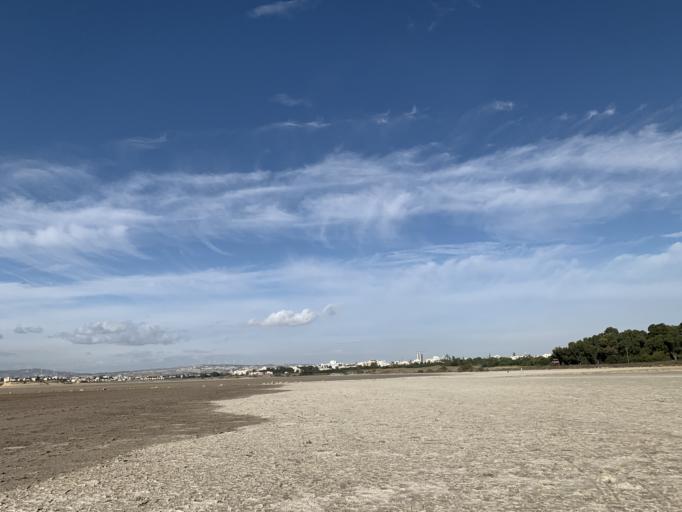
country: CY
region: Larnaka
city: Larnaca
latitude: 34.9040
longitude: 33.6209
